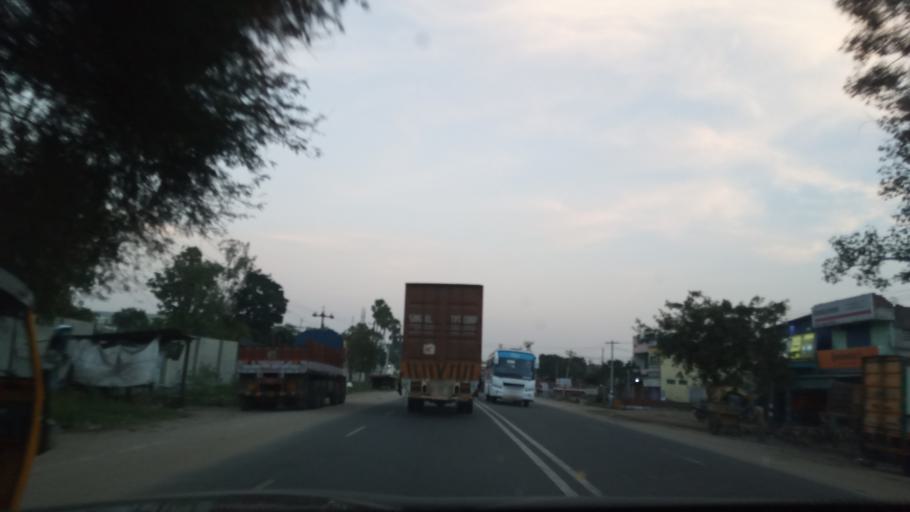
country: IN
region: Tamil Nadu
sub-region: Vellore
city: Walajapet
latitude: 12.9287
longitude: 79.3440
